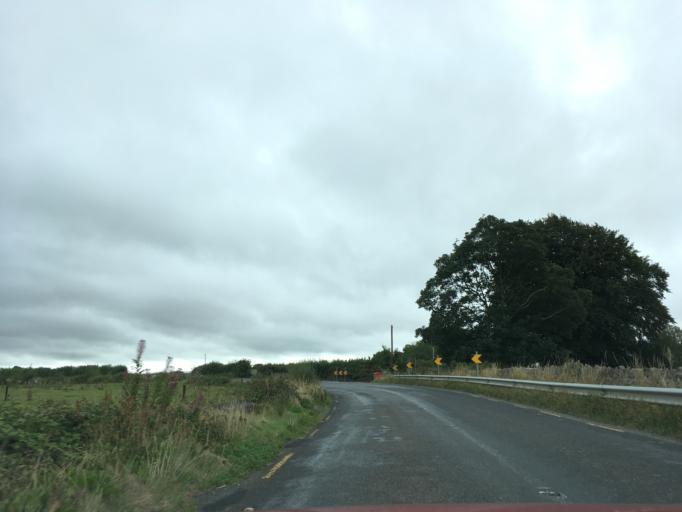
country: IE
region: Munster
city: Cashel
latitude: 52.4536
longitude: -7.8161
